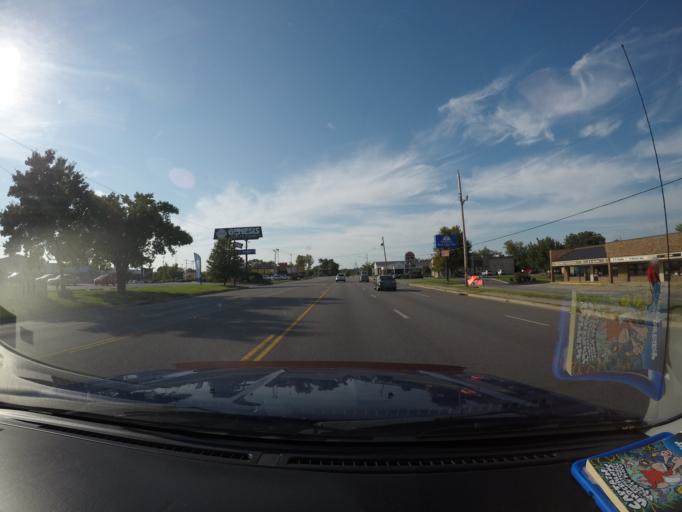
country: US
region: Kansas
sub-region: Leavenworth County
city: Leavenworth
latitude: 39.2868
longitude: -94.9055
